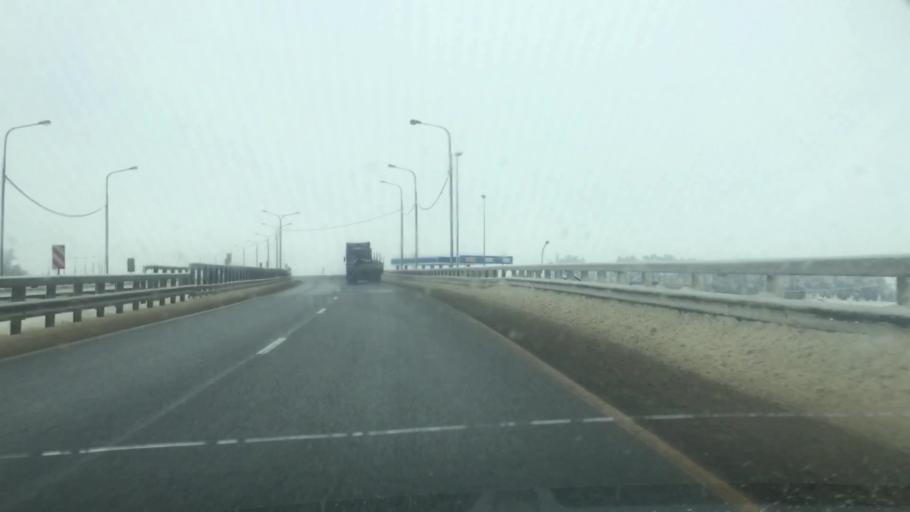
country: RU
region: Lipetsk
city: Yelets
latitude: 52.5450
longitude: 38.7196
